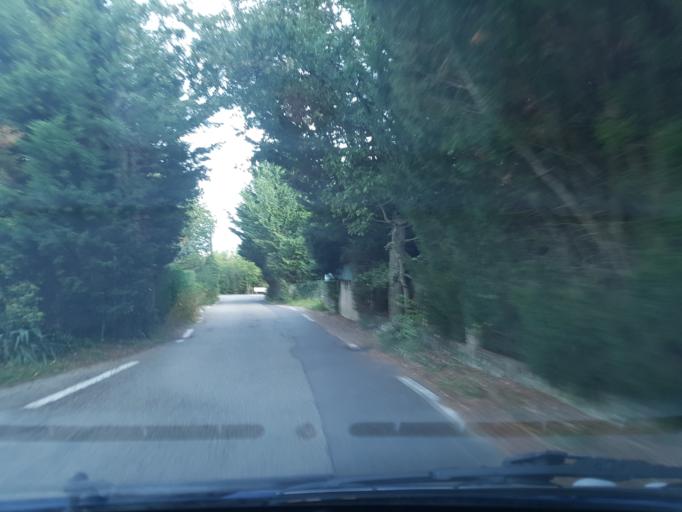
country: FR
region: Rhone-Alpes
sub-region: Departement du Rhone
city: Saint-Genis-les-Ollieres
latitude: 45.7732
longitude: 4.7212
